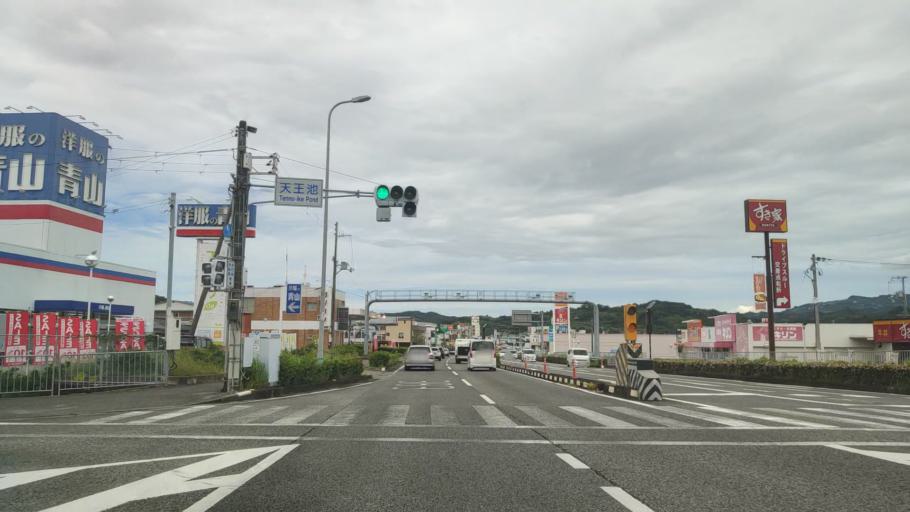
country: JP
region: Wakayama
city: Tanabe
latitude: 33.7378
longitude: 135.3961
